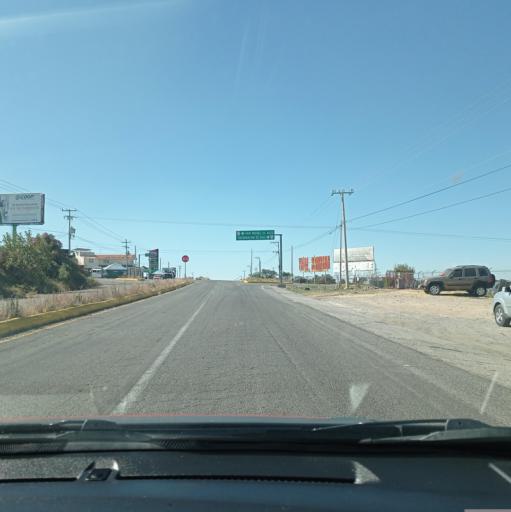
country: MX
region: Jalisco
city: San Miguel el Alto
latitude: 21.0142
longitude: -102.3214
